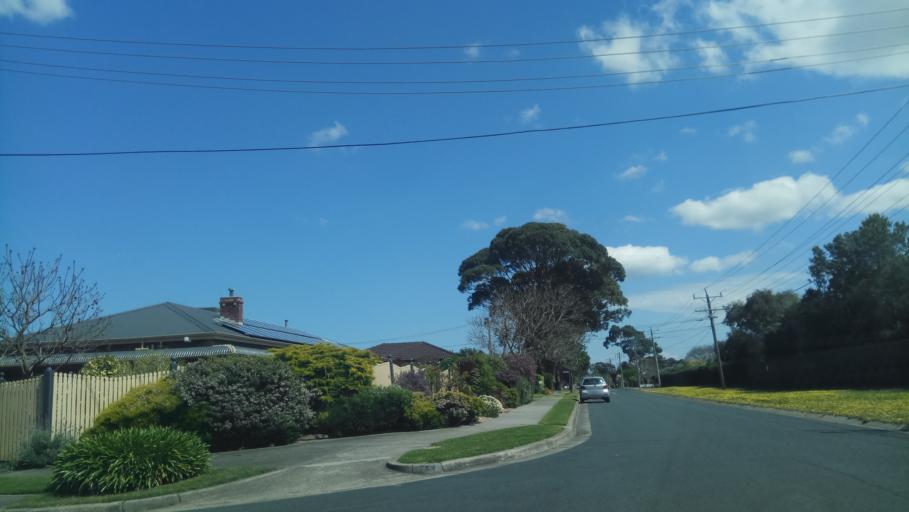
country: AU
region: Victoria
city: Heatherton
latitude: -37.9639
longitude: 145.0856
